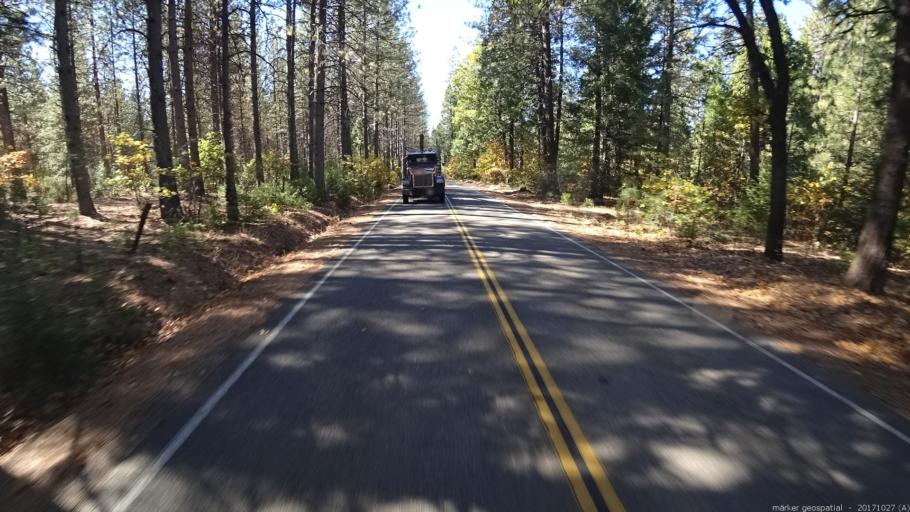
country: US
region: California
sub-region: Shasta County
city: Shingletown
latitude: 40.7093
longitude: -121.9646
